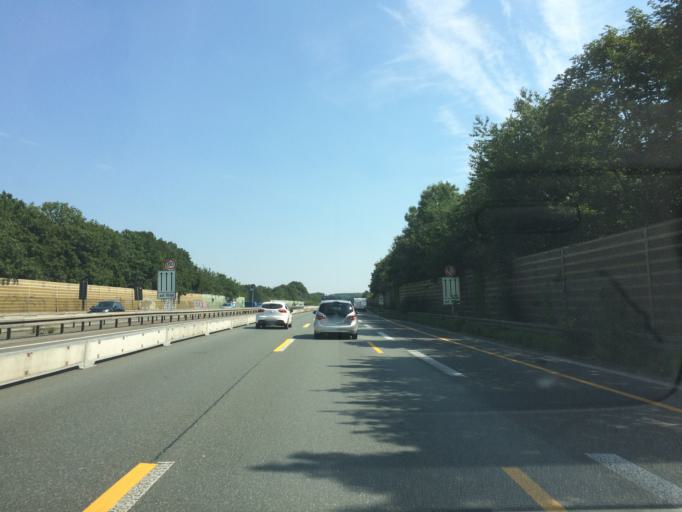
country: DE
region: North Rhine-Westphalia
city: Lunen
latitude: 51.5788
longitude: 7.5024
